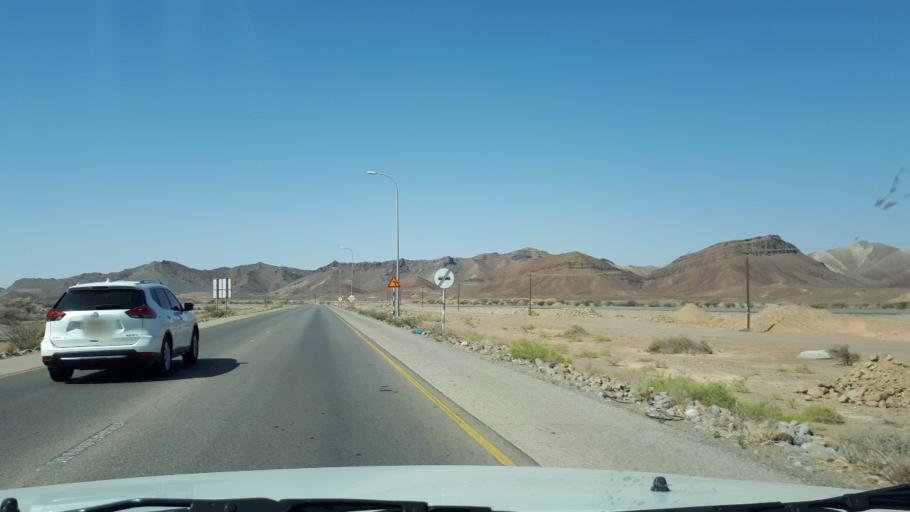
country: OM
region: Ash Sharqiyah
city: Sur
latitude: 22.3692
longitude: 59.3158
